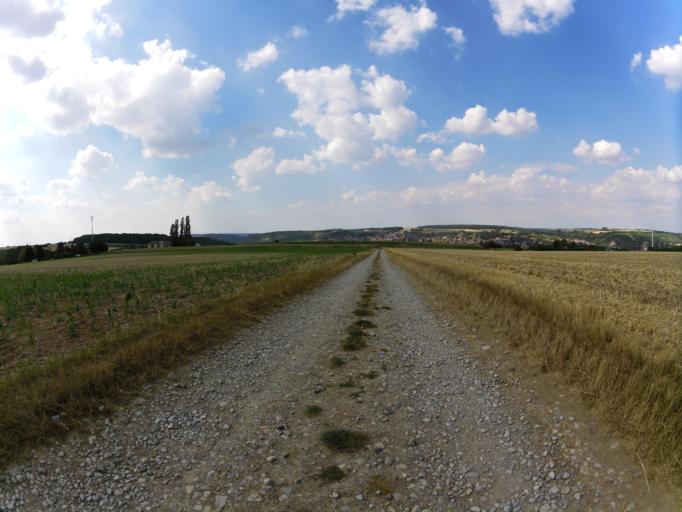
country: DE
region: Bavaria
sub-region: Regierungsbezirk Unterfranken
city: Ochsenfurt
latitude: 49.6547
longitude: 10.0671
